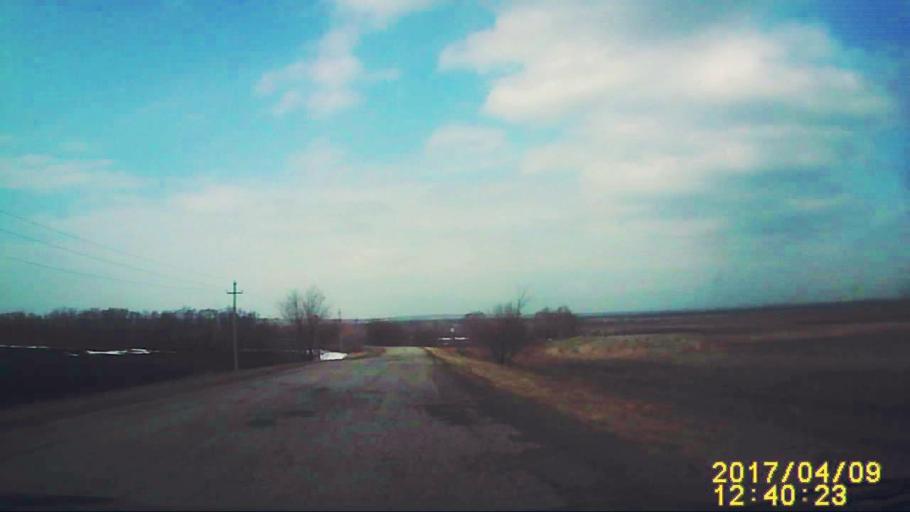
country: RU
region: Ulyanovsk
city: Ignatovka
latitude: 54.0025
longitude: 47.9473
